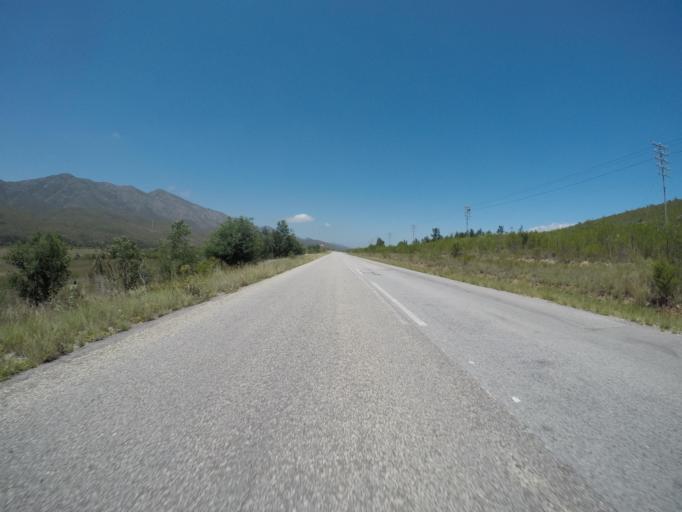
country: ZA
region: Eastern Cape
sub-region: Cacadu District Municipality
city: Kareedouw
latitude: -33.9069
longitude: 24.1535
